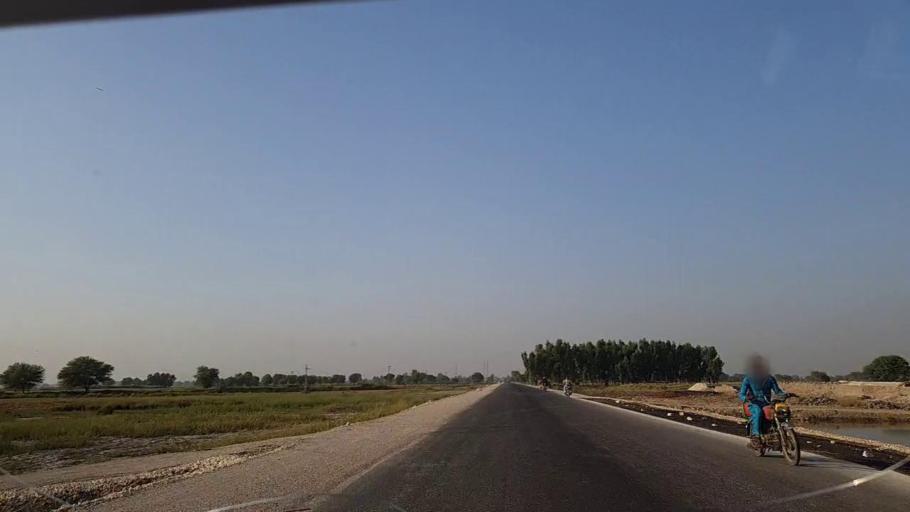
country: PK
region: Sindh
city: Rustam jo Goth
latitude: 27.9499
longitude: 68.8094
